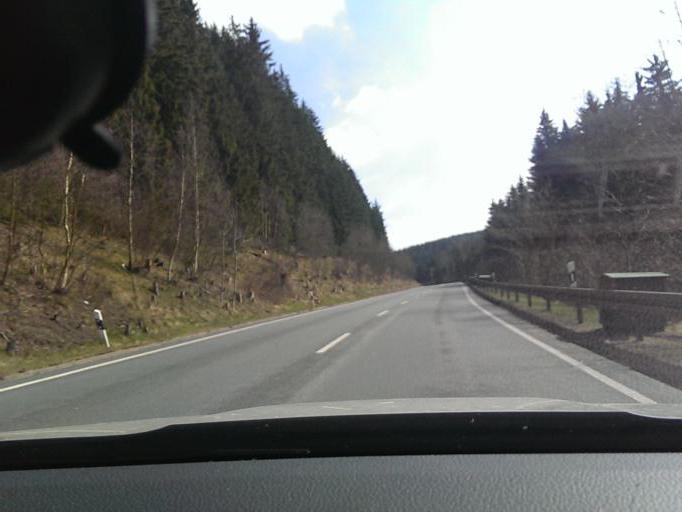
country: DE
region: Thuringia
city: Luisenthal
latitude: 50.7664
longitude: 10.7335
